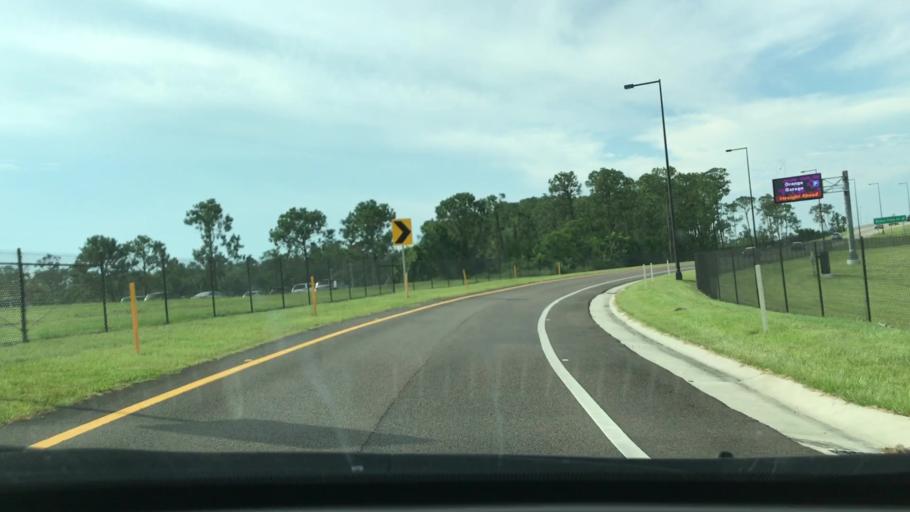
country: US
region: Florida
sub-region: Osceola County
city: Celebration
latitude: 28.3642
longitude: -81.5240
